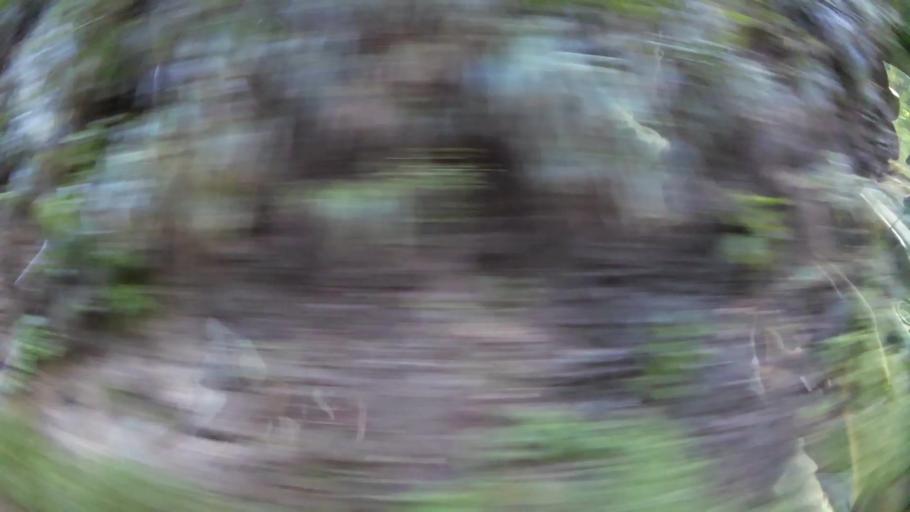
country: DM
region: Saint Andrew
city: Calibishie
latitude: 15.5914
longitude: -61.3904
